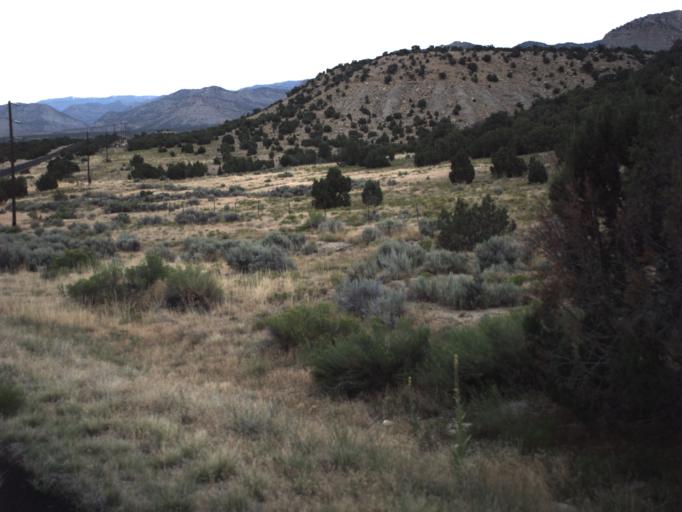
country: US
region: Utah
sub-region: Carbon County
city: East Carbon City
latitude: 39.4888
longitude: -110.4044
